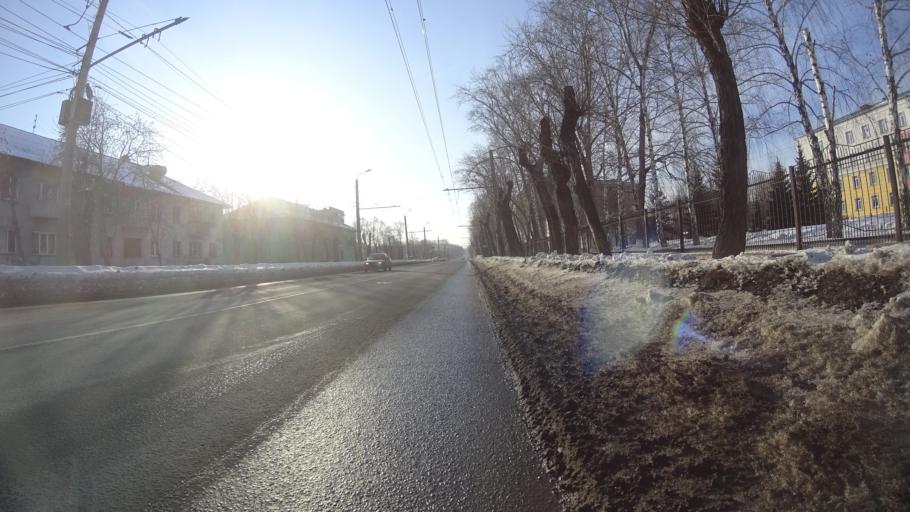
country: RU
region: Chelyabinsk
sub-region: Gorod Chelyabinsk
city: Chelyabinsk
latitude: 55.1825
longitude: 61.4522
